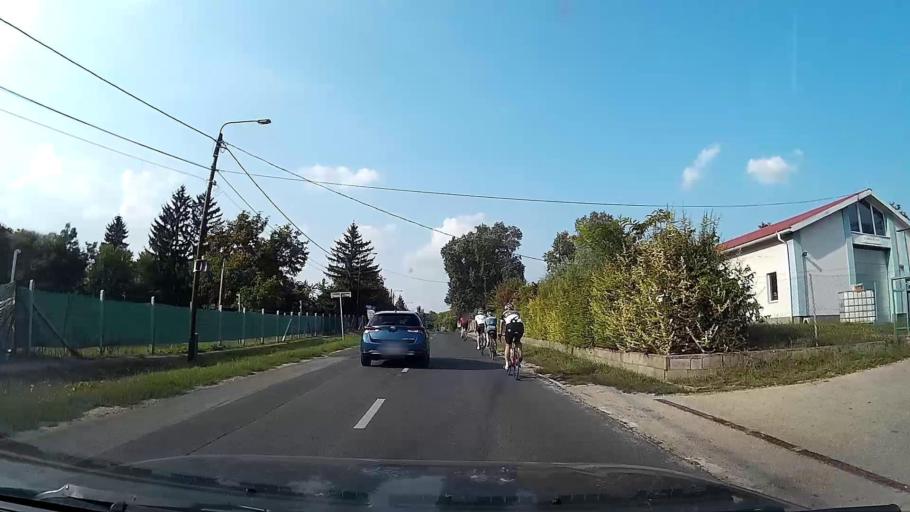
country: HU
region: Pest
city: Pomaz
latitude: 47.6343
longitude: 19.0399
